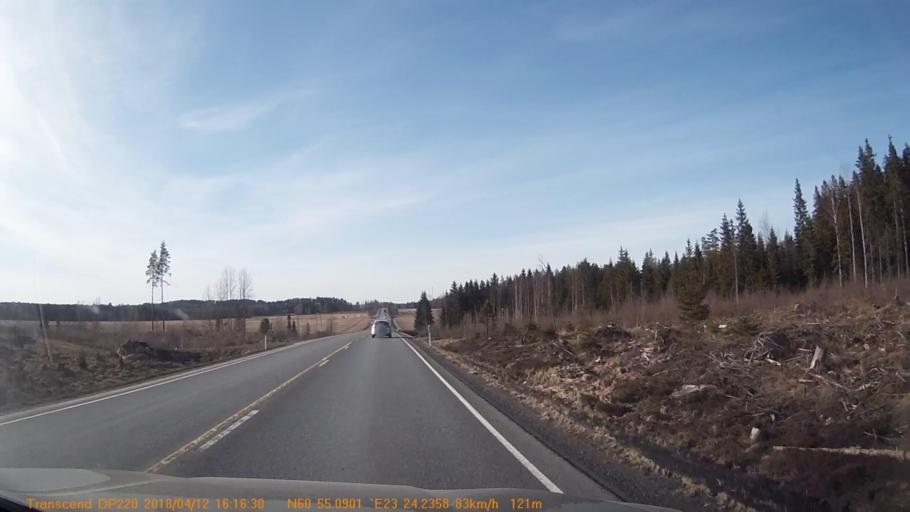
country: FI
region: Haeme
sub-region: Forssa
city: Humppila
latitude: 60.9182
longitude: 23.4038
